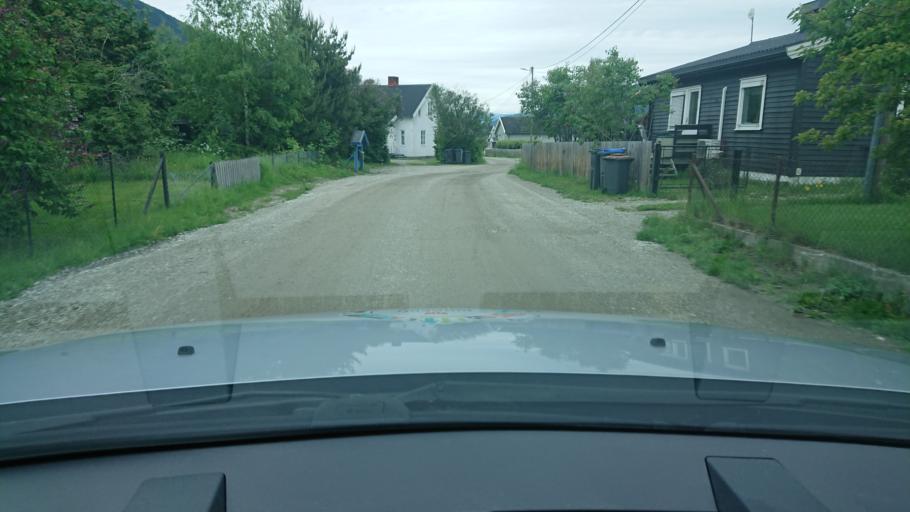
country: NO
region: Oppland
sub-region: Ringebu
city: Ringebu
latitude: 61.5285
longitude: 10.1308
